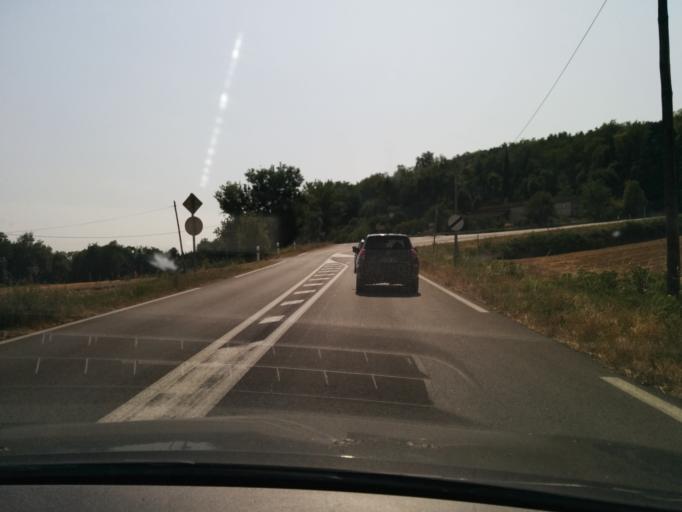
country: FR
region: Midi-Pyrenees
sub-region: Departement du Tarn
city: Albi
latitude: 43.9480
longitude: 2.1189
